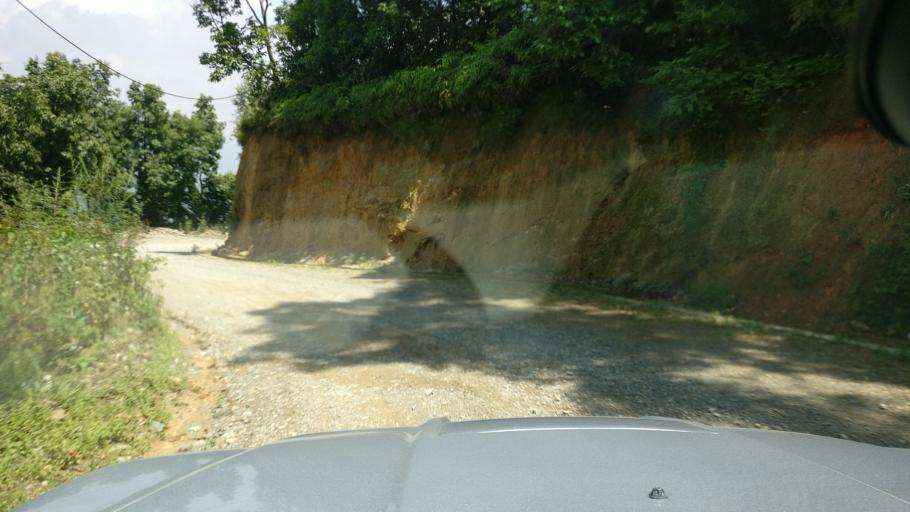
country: NP
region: Central Region
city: Kirtipur
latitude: 27.7070
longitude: 85.2522
